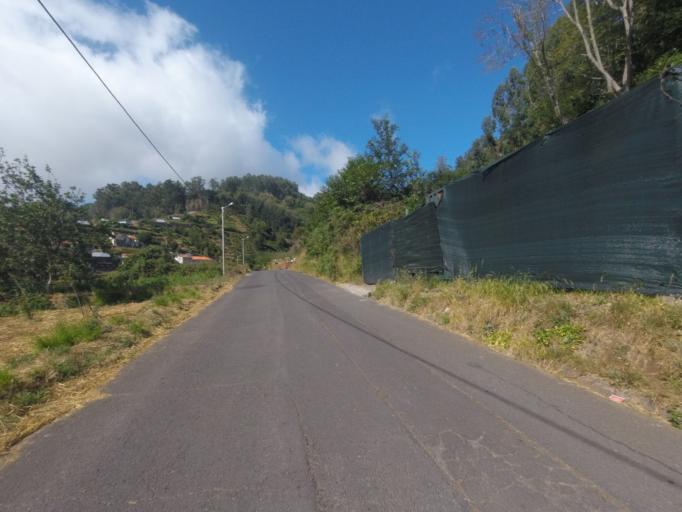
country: PT
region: Madeira
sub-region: Ribeira Brava
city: Campanario
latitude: 32.7010
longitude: -17.0162
